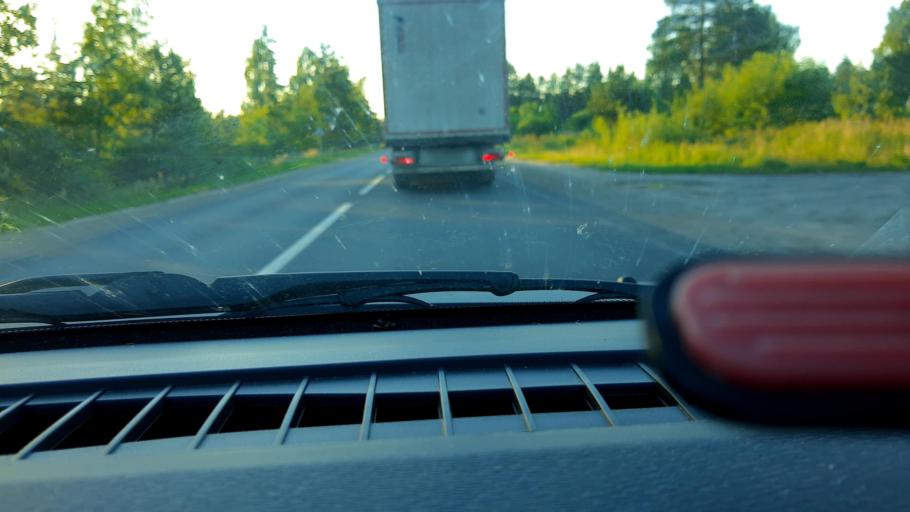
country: RU
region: Nizjnij Novgorod
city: Uren'
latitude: 57.3452
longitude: 45.7083
